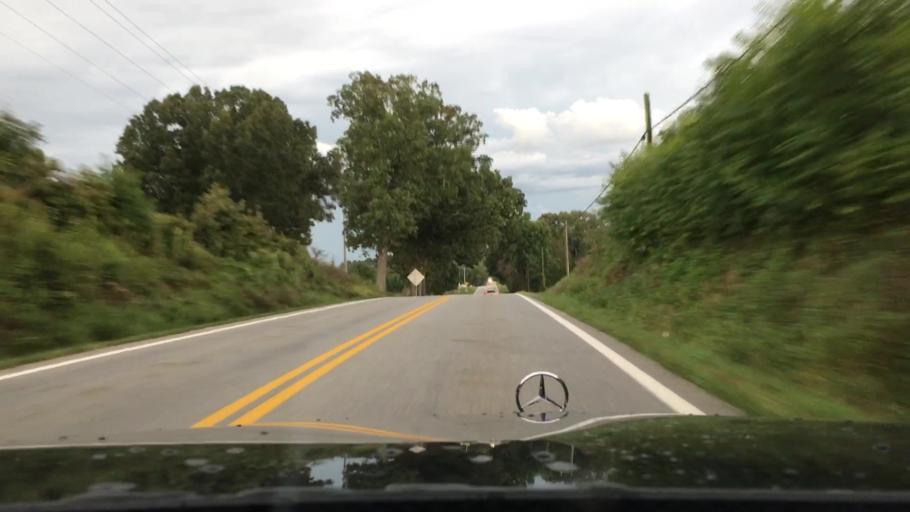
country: US
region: Virginia
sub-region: Amherst County
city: Amherst
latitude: 37.6287
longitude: -79.0182
